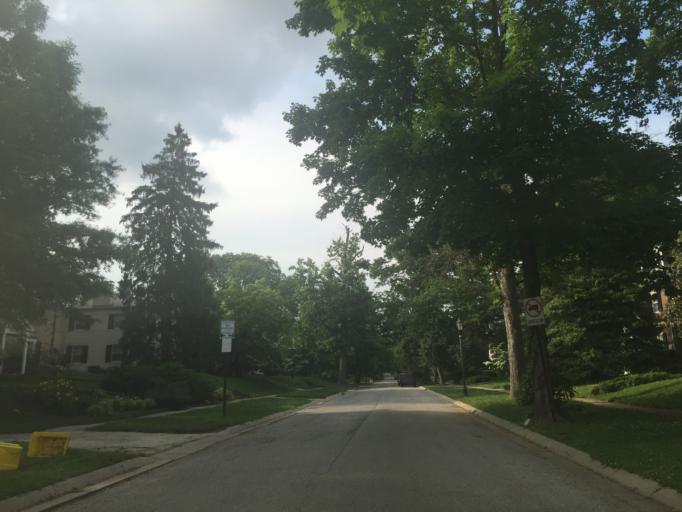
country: US
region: Maryland
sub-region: City of Baltimore
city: Baltimore
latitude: 39.3343
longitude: -76.6107
